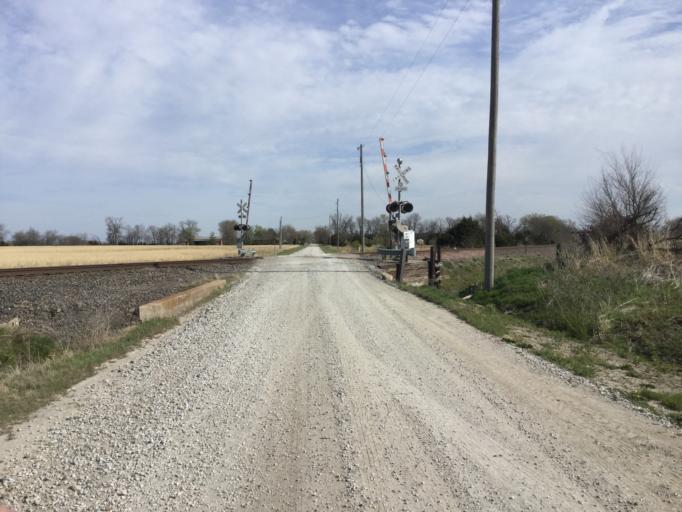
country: US
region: Kansas
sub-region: Montgomery County
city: Independence
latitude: 37.3024
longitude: -95.7290
